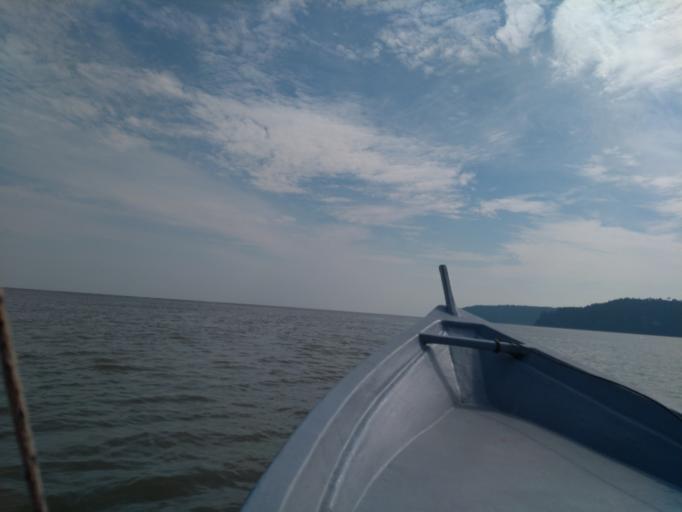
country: MY
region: Sarawak
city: Kuching
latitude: 1.7035
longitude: 110.4300
